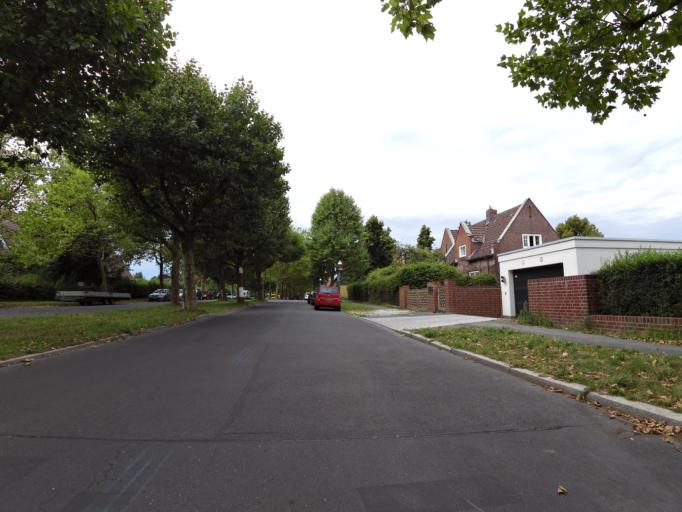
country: DE
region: Berlin
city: Schmargendorf
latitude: 52.4689
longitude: 13.2988
